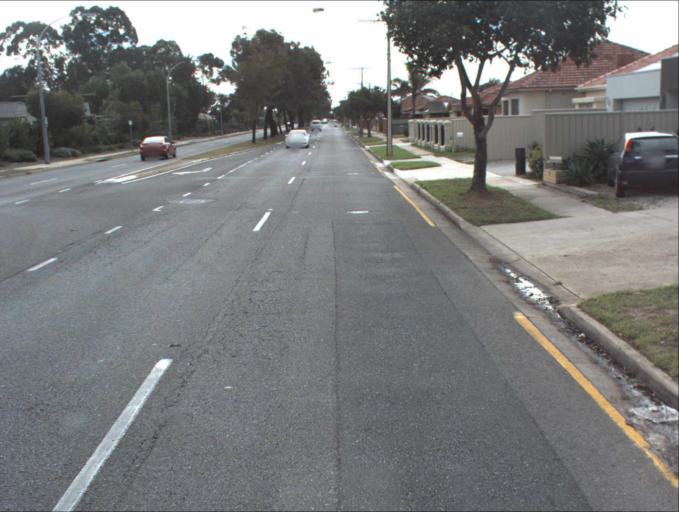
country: AU
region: South Australia
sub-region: Charles Sturt
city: Royal Park
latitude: -34.8769
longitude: 138.5036
